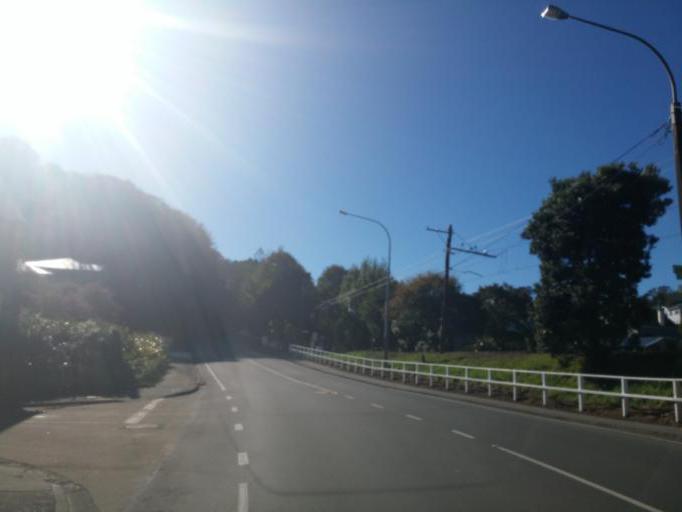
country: NZ
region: Wellington
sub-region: Wellington City
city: Wellington
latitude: -41.2409
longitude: 174.7943
